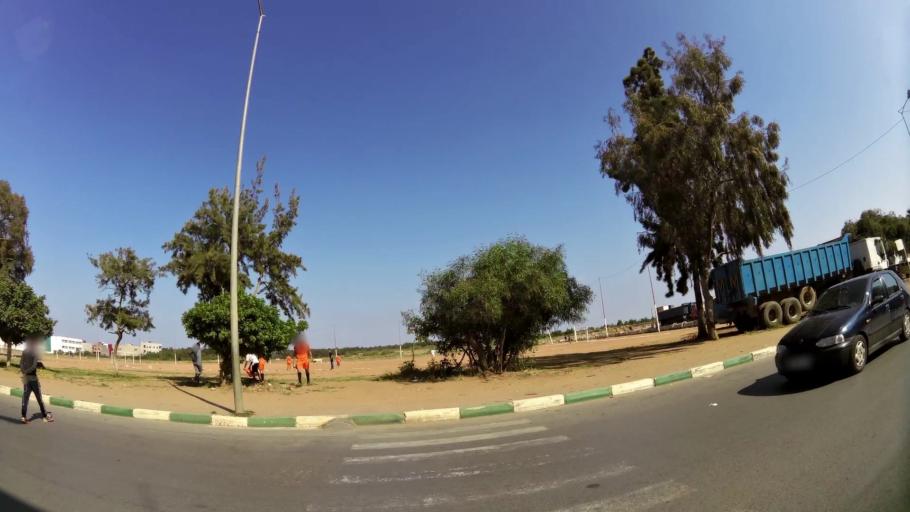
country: MA
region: Rabat-Sale-Zemmour-Zaer
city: Sale
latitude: 34.0607
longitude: -6.7675
